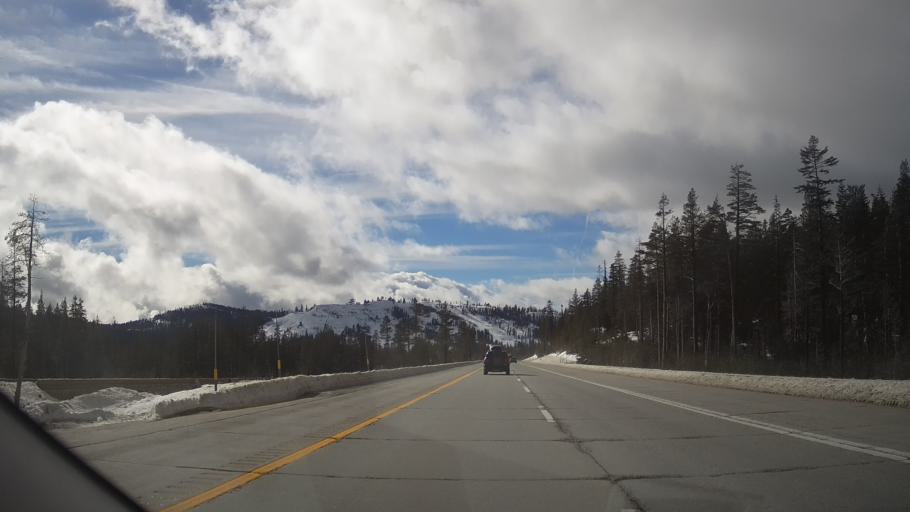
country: US
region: California
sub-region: Nevada County
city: Truckee
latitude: 39.3305
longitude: -120.3653
